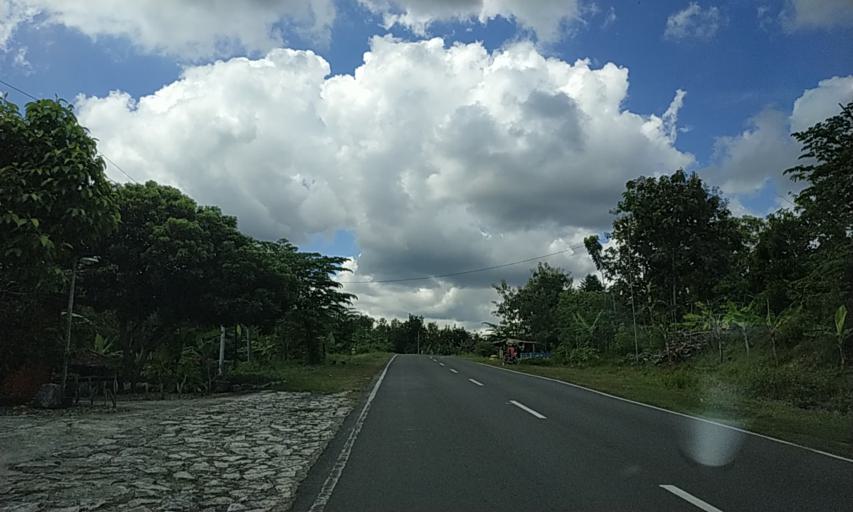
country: ID
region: East Java
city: Krajan
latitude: -8.0446
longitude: 110.9474
